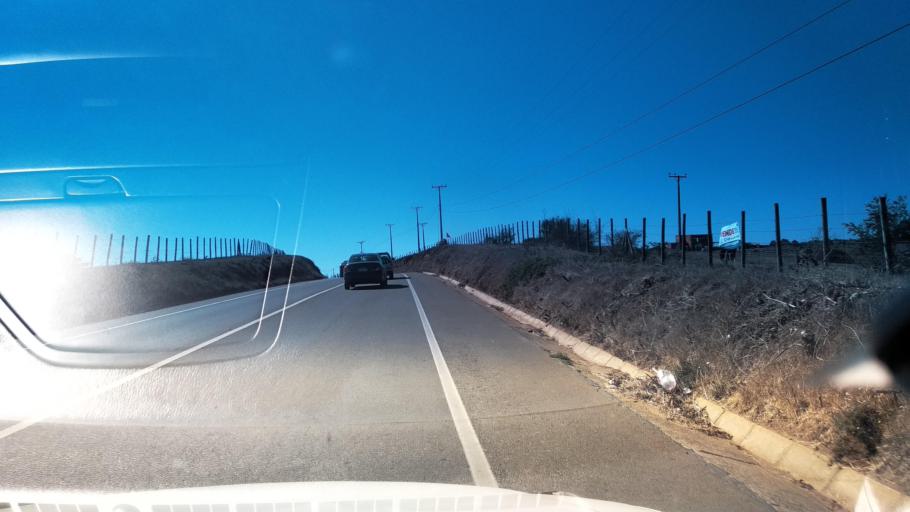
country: CL
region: O'Higgins
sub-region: Provincia de Colchagua
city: Santa Cruz
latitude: -34.4403
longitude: -72.0327
